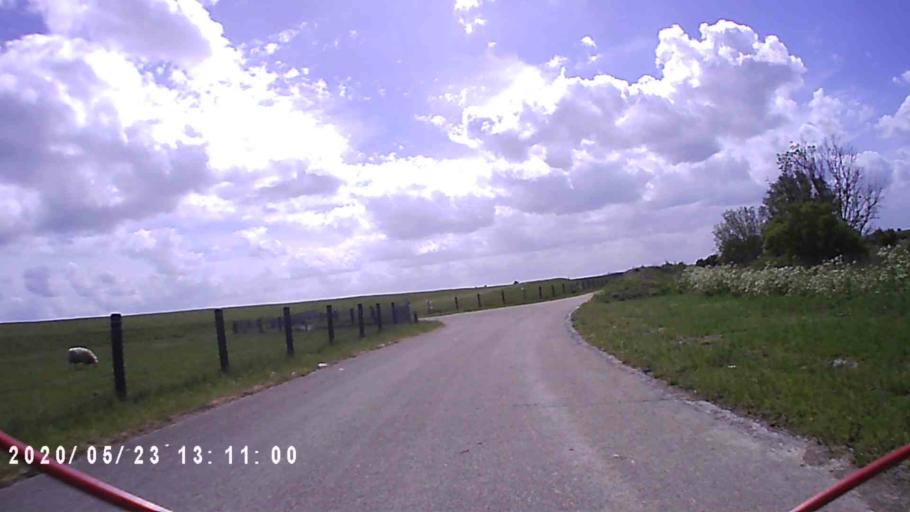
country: DE
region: Lower Saxony
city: Emden
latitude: 53.3010
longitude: 7.0829
